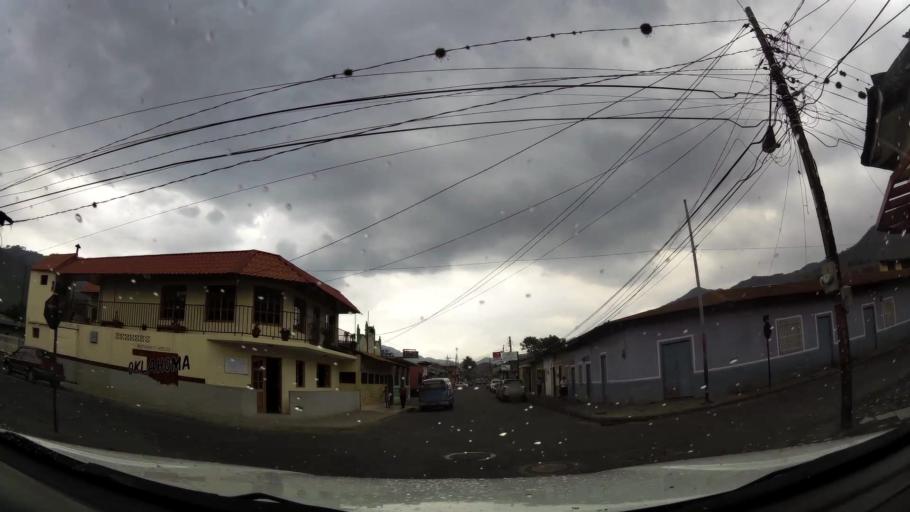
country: NI
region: Jinotega
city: Jinotega
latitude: 13.0960
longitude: -86.0009
